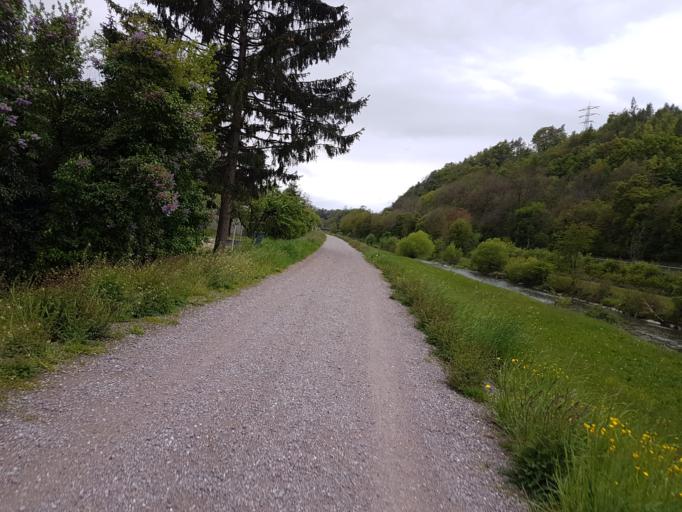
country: DE
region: Baden-Wuerttemberg
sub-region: Freiburg Region
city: Wutoschingen
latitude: 47.6651
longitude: 8.3695
